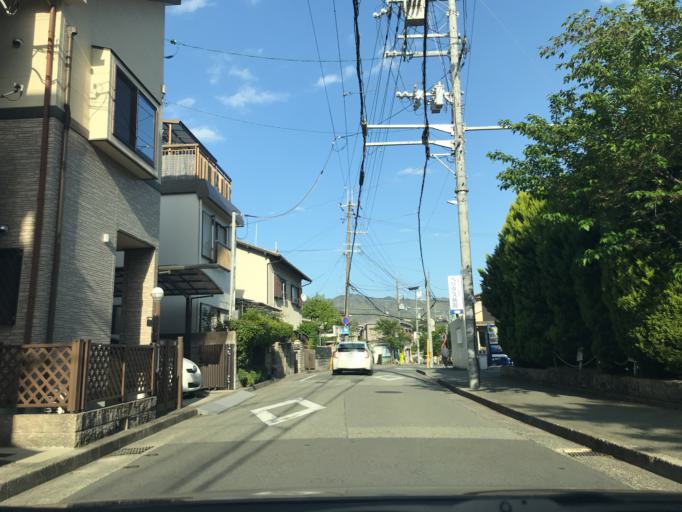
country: JP
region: Osaka
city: Ikeda
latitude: 34.8615
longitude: 135.4106
